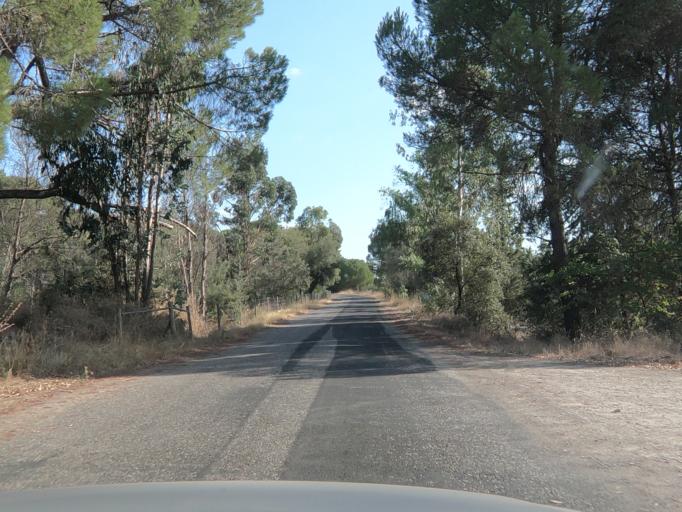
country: PT
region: Setubal
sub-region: Alcacer do Sal
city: Alcacer do Sal
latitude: 38.2515
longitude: -8.2977
